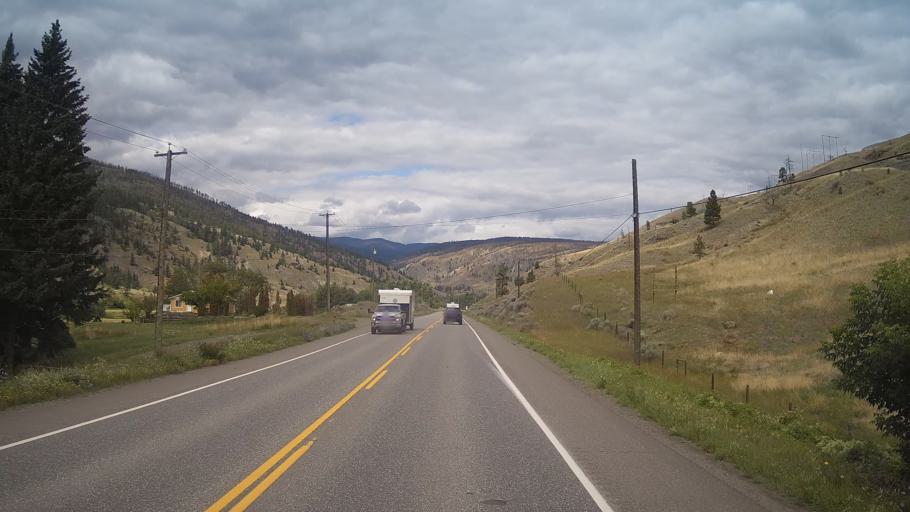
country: CA
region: British Columbia
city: Cache Creek
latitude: 50.9535
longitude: -121.4371
